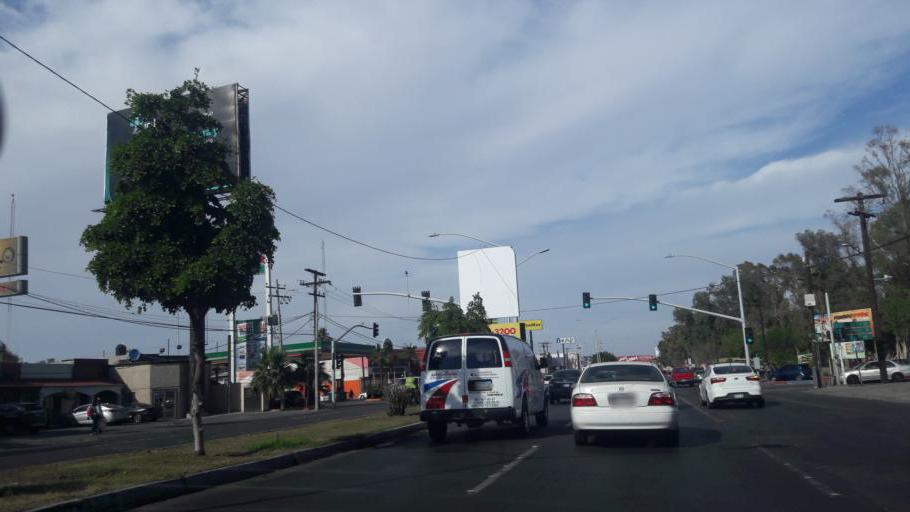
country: MX
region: Baja California
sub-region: Mexicali
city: Mexicali
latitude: 32.6300
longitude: -115.4457
